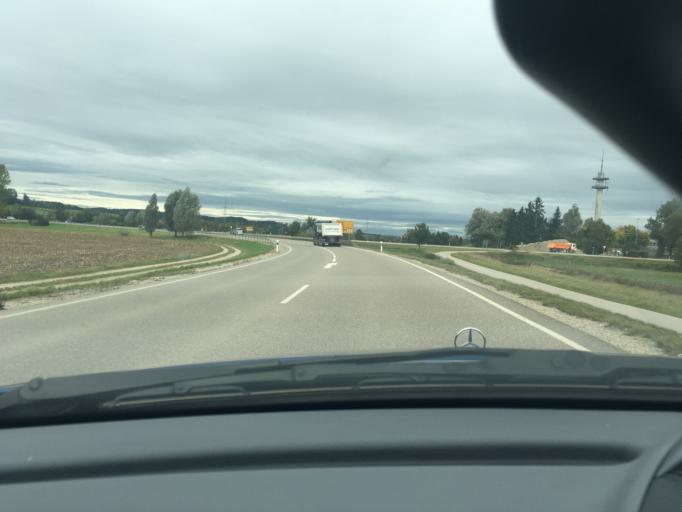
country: DE
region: Bavaria
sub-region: Swabia
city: Gablingen
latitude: 48.4274
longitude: 10.8267
